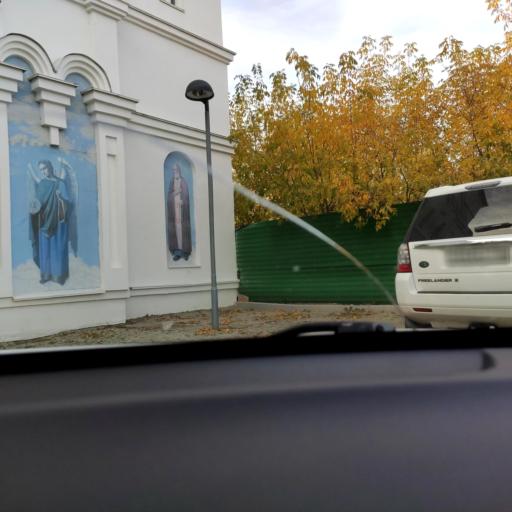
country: RU
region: Tatarstan
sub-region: Gorod Kazan'
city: Kazan
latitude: 55.8079
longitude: 49.0587
